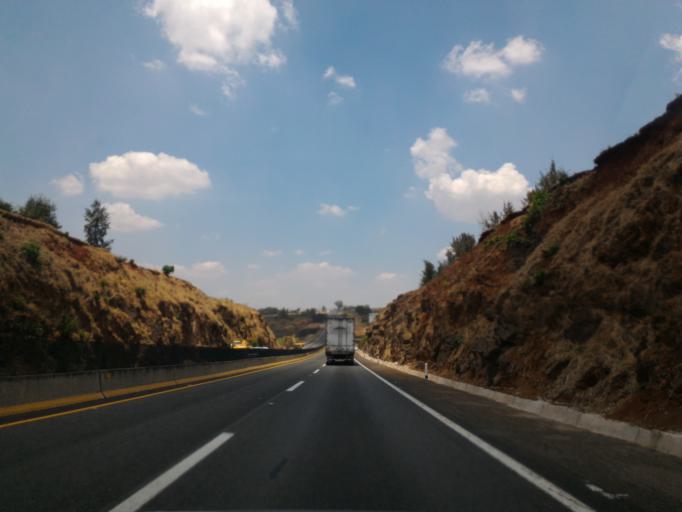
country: MX
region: Jalisco
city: Tepatitlan de Morelos
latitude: 20.8033
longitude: -102.8110
